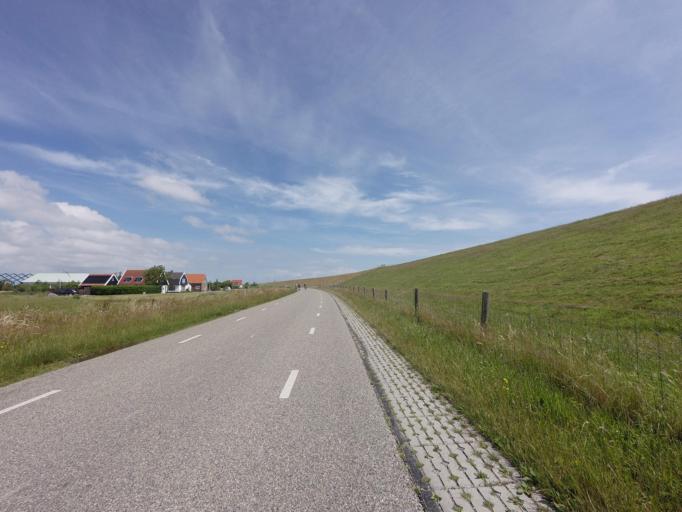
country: NL
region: North Holland
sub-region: Gemeente Texel
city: Den Burg
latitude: 53.0729
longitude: 4.8868
